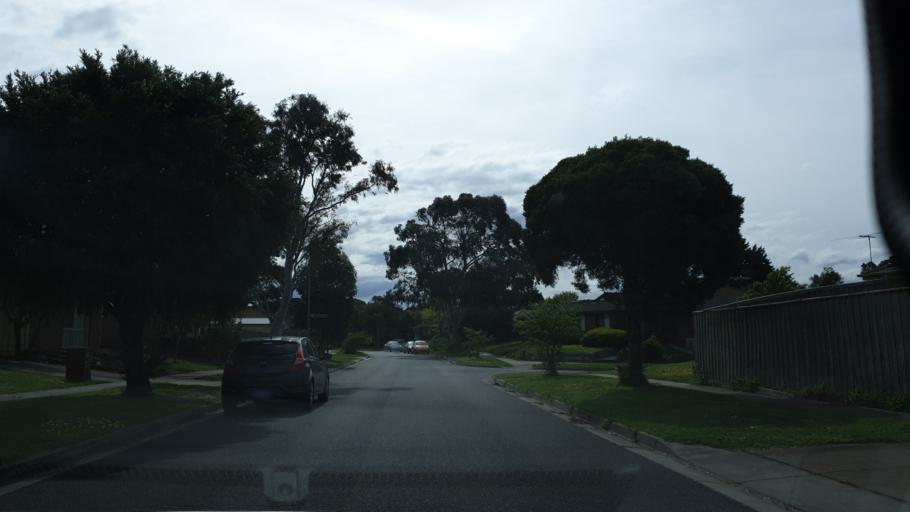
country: AU
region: Victoria
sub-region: Casey
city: Cranbourne North
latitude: -38.0780
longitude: 145.2885
